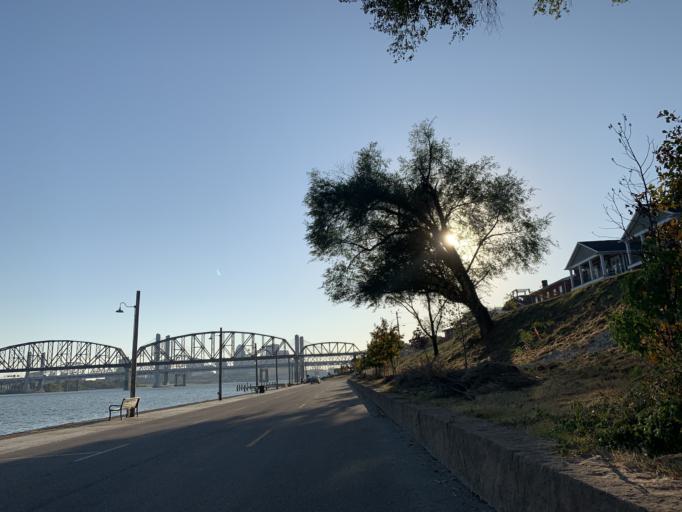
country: US
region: Indiana
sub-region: Clark County
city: Jeffersonville
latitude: 38.2706
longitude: -85.7359
